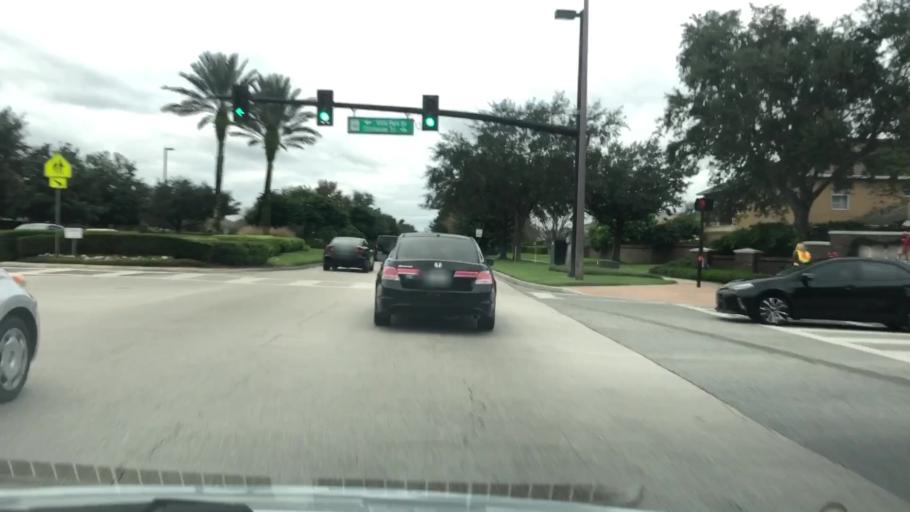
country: US
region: Florida
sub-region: Orange County
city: Conway
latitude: 28.4687
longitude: -81.2678
